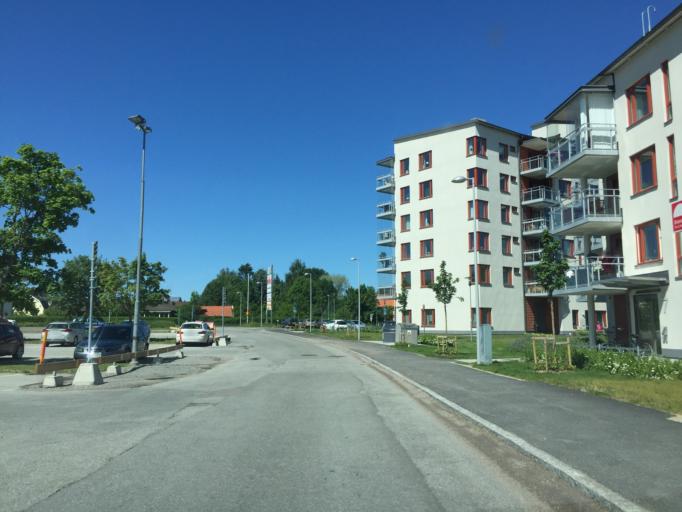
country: SE
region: OErebro
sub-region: Orebro Kommun
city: Orebro
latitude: 59.2475
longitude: 15.1684
